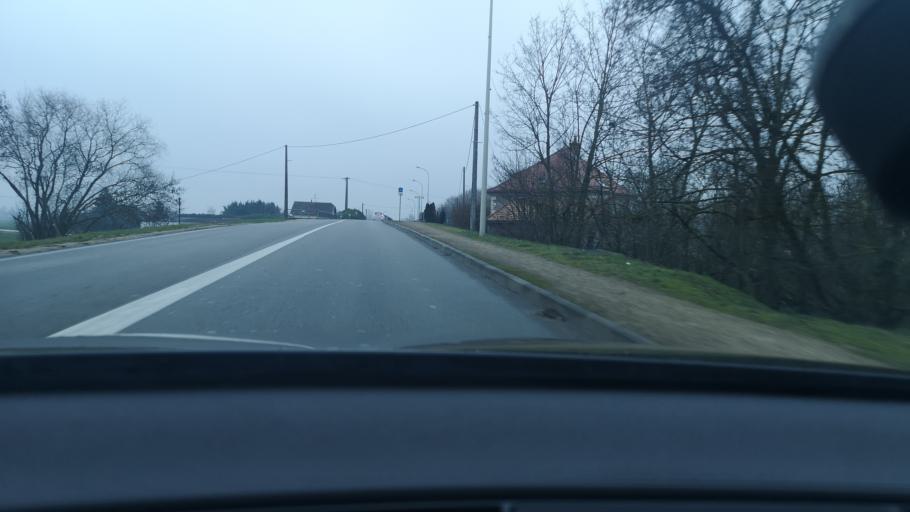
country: FR
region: Bourgogne
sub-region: Departement de la Cote-d'Or
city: Longvic
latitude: 47.2775
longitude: 5.0623
